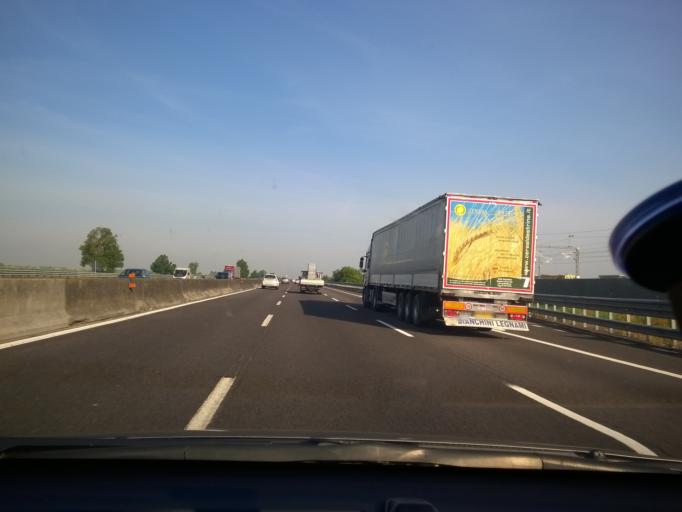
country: IT
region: Emilia-Romagna
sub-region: Provincia di Reggio Emilia
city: Campegine
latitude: 44.7577
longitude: 10.5416
